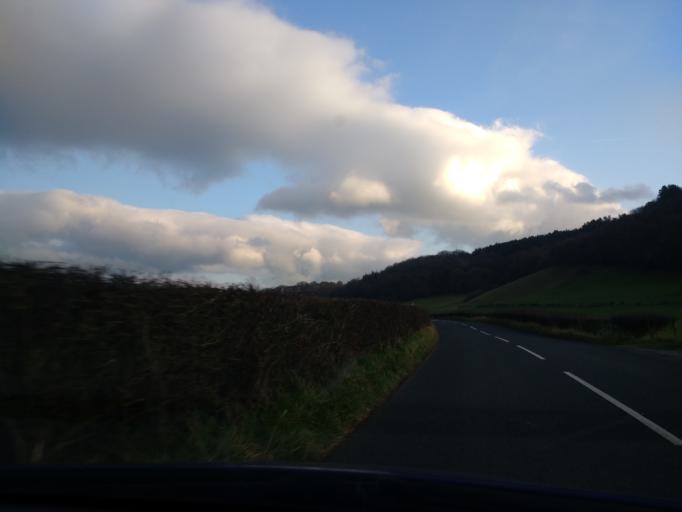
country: GB
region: England
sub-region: Lancashire
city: Caton
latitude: 54.0561
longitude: -2.7303
